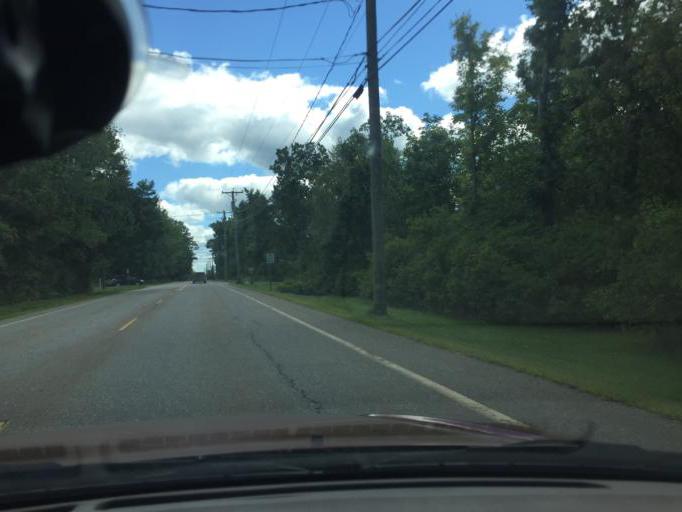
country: US
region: Connecticut
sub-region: Litchfield County
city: Litchfield
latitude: 41.8039
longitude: -73.2147
